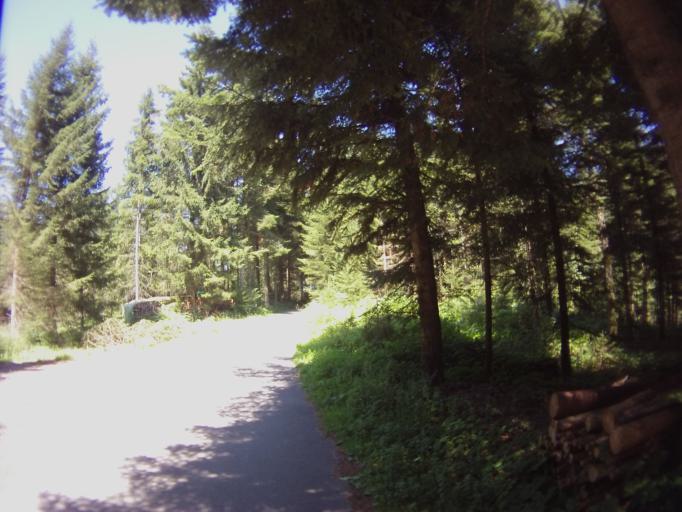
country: CH
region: Schwyz
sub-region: Bezirk Hoefe
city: Feusisberg
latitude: 47.1741
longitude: 8.7550
